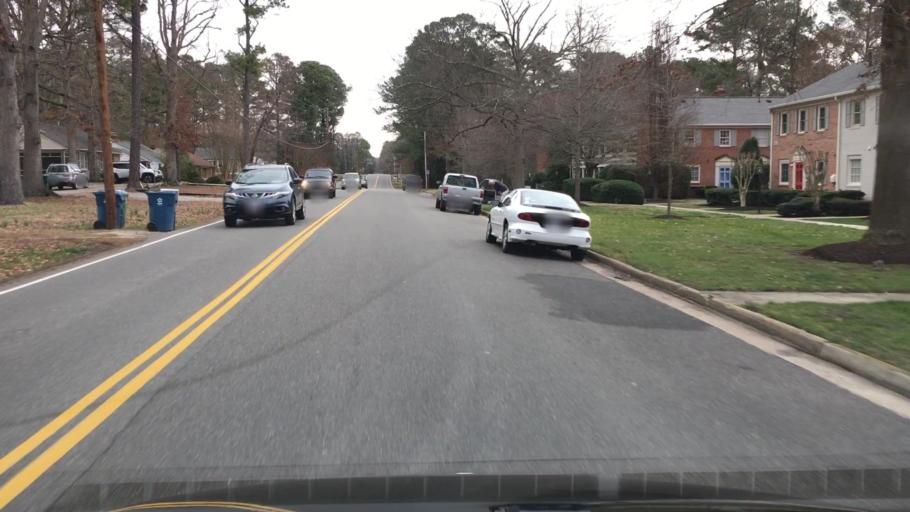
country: US
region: Virginia
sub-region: Henrico County
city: Tuckahoe
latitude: 37.5883
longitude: -77.5841
